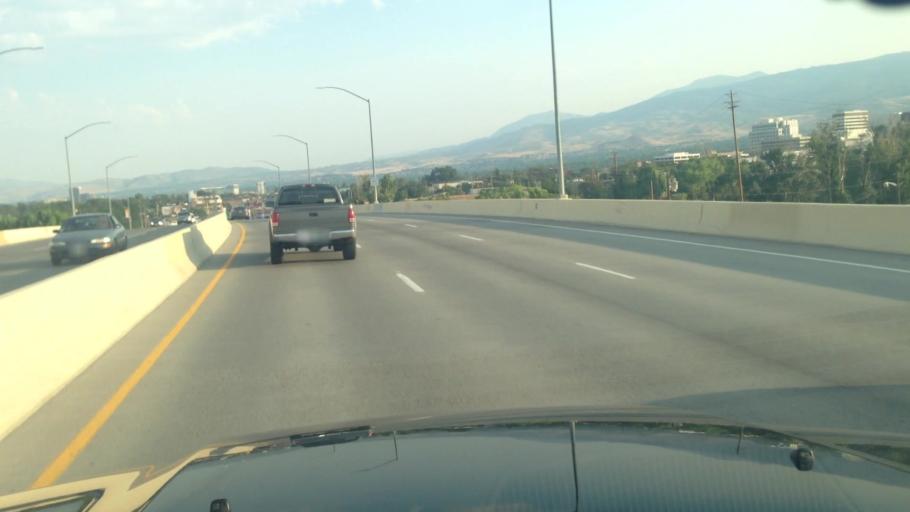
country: US
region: Nevada
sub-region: Washoe County
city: Reno
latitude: 39.5316
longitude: -119.8033
